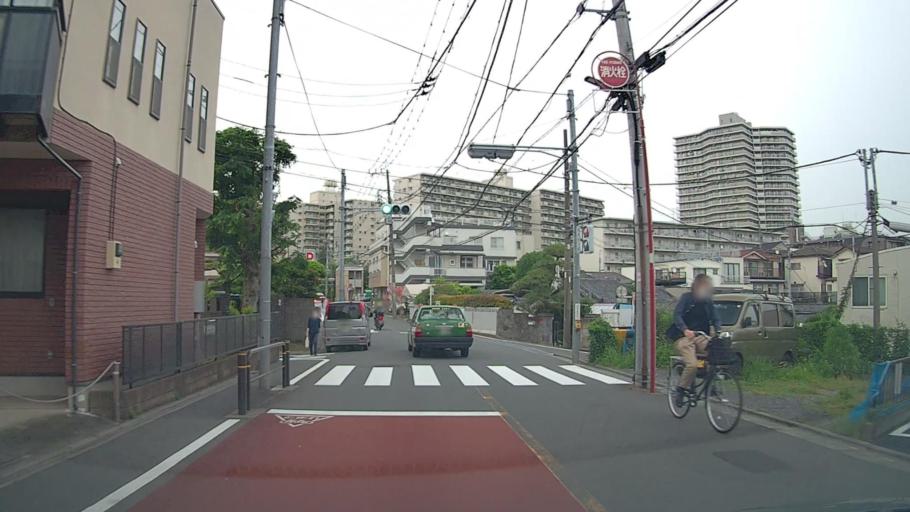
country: JP
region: Saitama
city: Shimotoda
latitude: 35.7728
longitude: 139.6768
